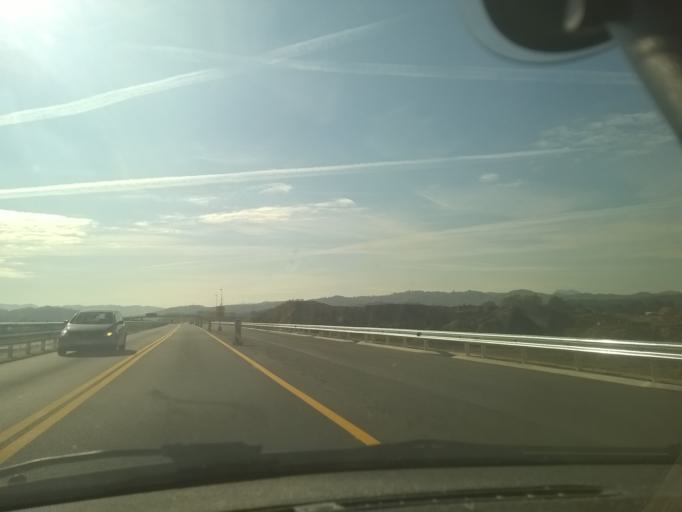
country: SI
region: Hajdina
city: Spodnja Hajdina
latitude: 46.3739
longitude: 15.8659
